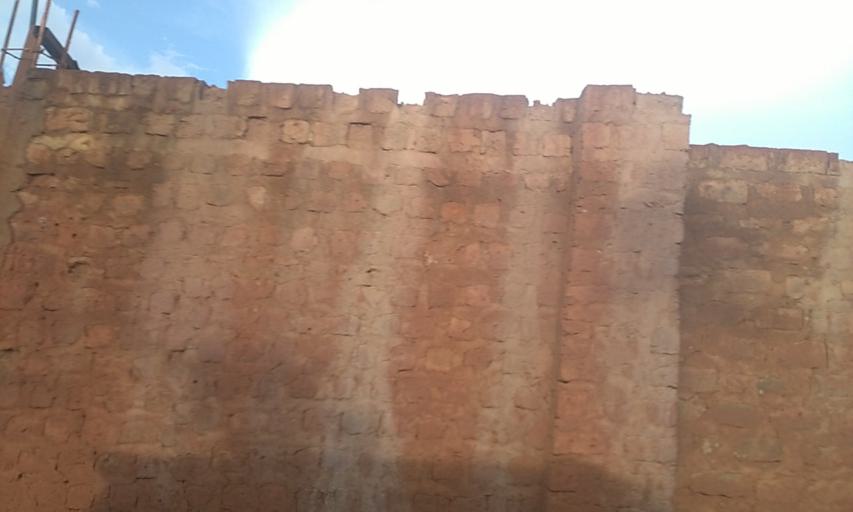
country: UG
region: Central Region
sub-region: Wakiso District
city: Kajansi
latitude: 0.2635
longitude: 32.5298
